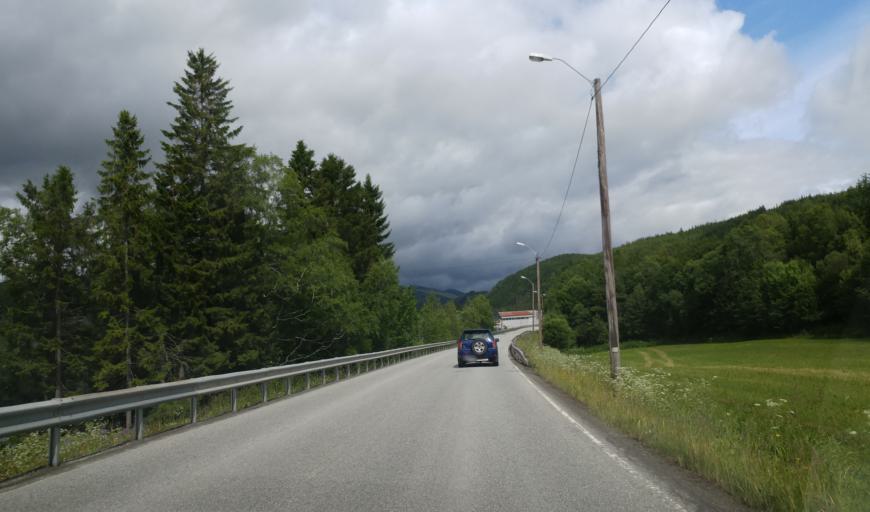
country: NO
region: Sor-Trondelag
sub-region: Selbu
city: Mebonden
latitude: 63.2742
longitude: 11.0774
